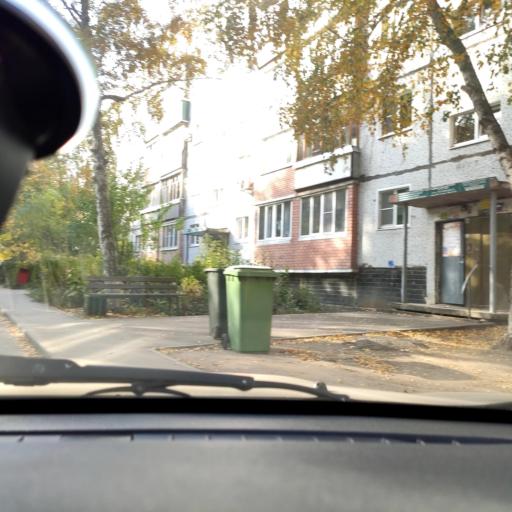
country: RU
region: Samara
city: Tol'yatti
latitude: 53.5118
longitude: 49.2653
